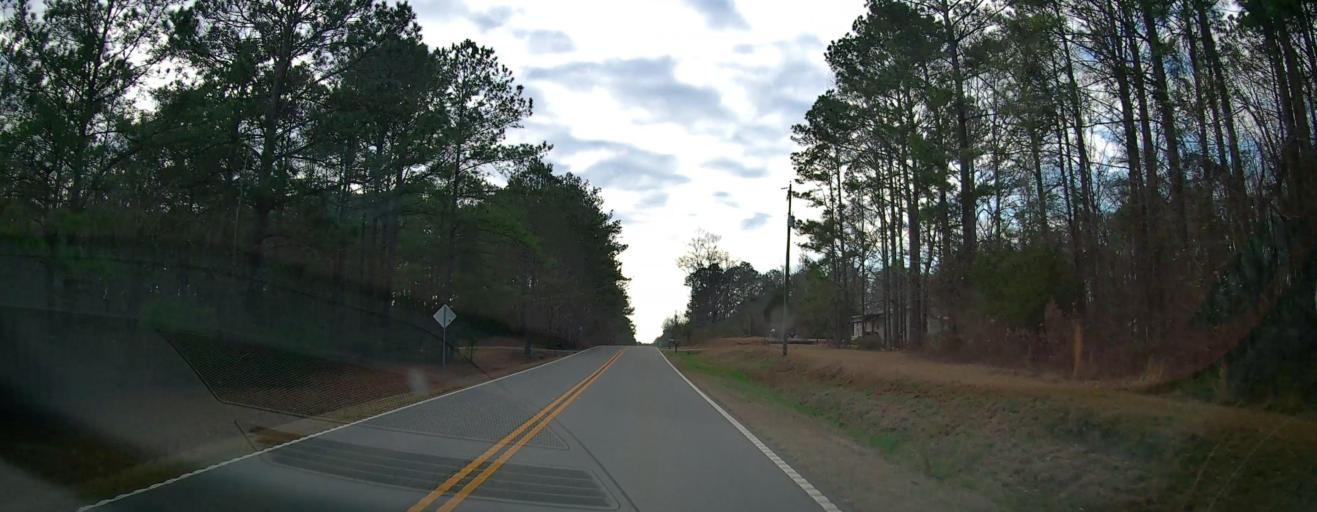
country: US
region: Georgia
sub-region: Harris County
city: Hamilton
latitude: 32.7031
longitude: -84.8249
